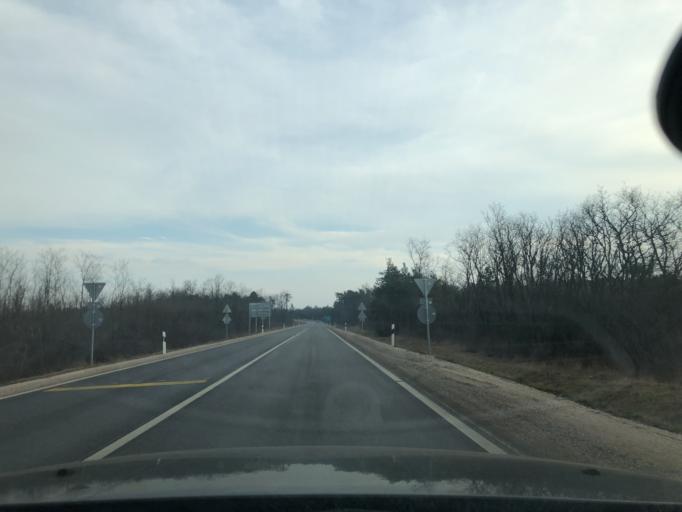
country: HU
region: Gyor-Moson-Sopron
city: Gyor
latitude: 47.7227
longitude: 17.7050
